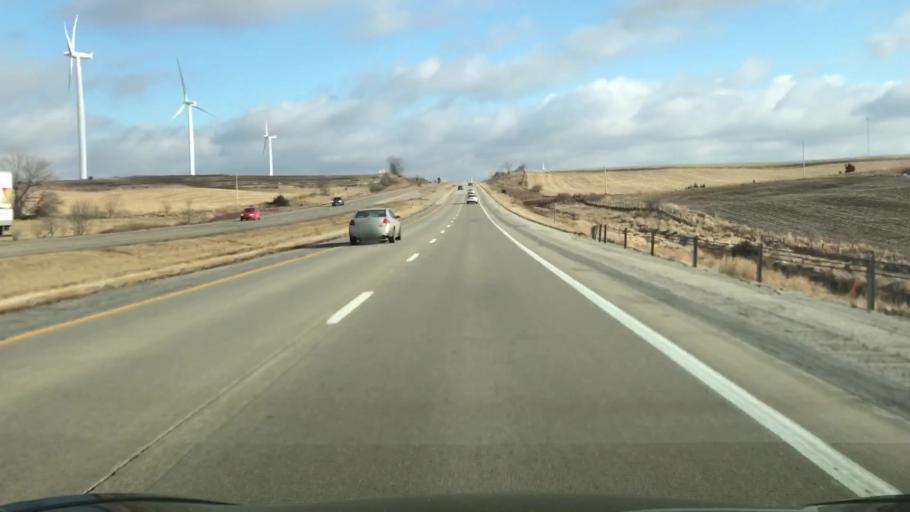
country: US
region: Iowa
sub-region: Guthrie County
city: Guthrie Center
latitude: 41.4968
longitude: -94.7033
